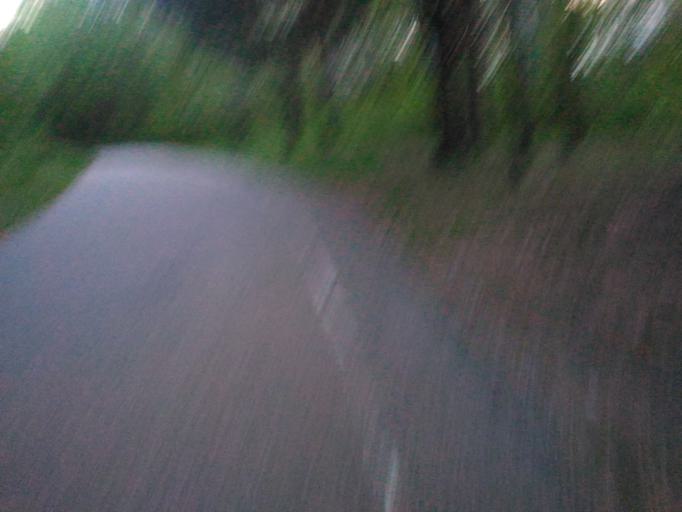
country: RU
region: Ulyanovsk
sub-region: Ulyanovskiy Rayon
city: Ulyanovsk
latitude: 54.2748
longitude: 48.3567
